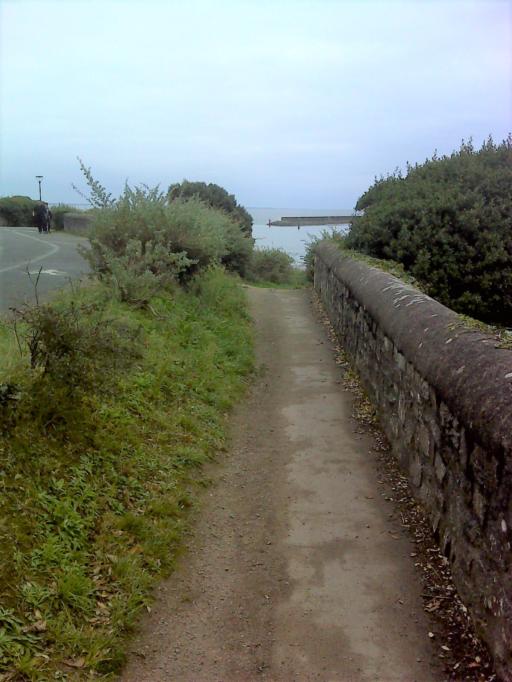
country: FR
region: Pays de la Loire
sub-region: Departement de la Loire-Atlantique
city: Pornic
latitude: 47.1099
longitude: -2.1068
